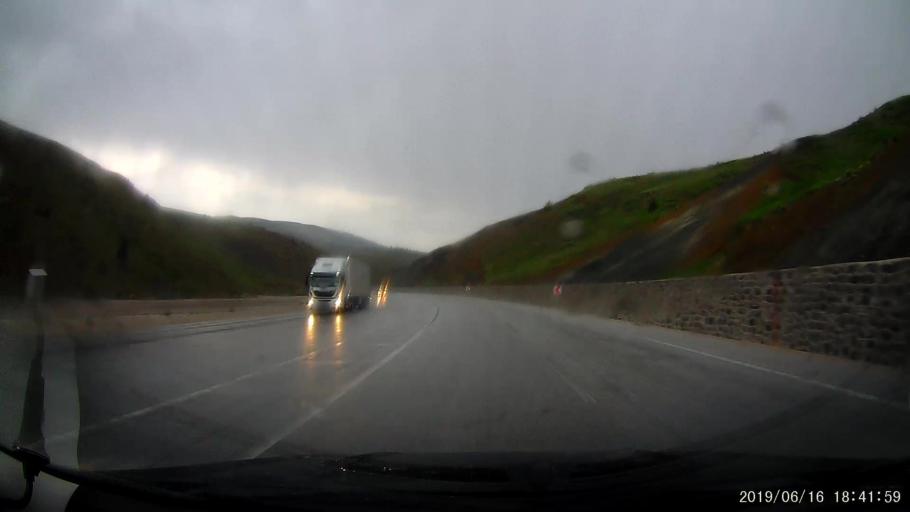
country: TR
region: Erzincan
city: Doganbeyli
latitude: 39.8728
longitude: 39.1180
